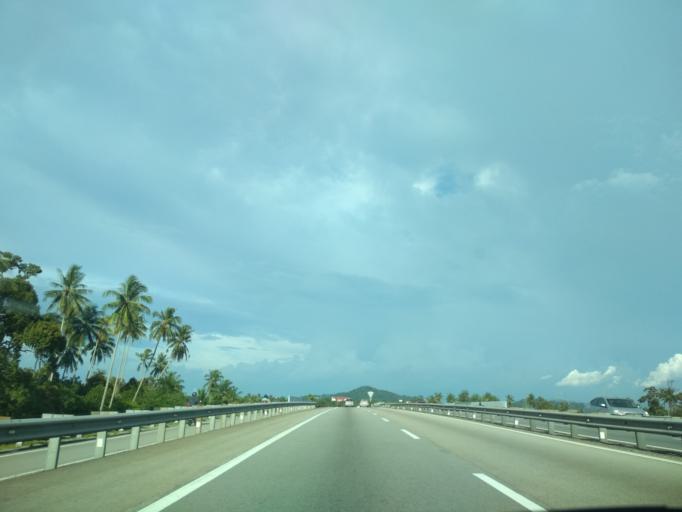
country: MY
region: Penang
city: Bukit Mertajam
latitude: 5.4026
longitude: 100.4711
